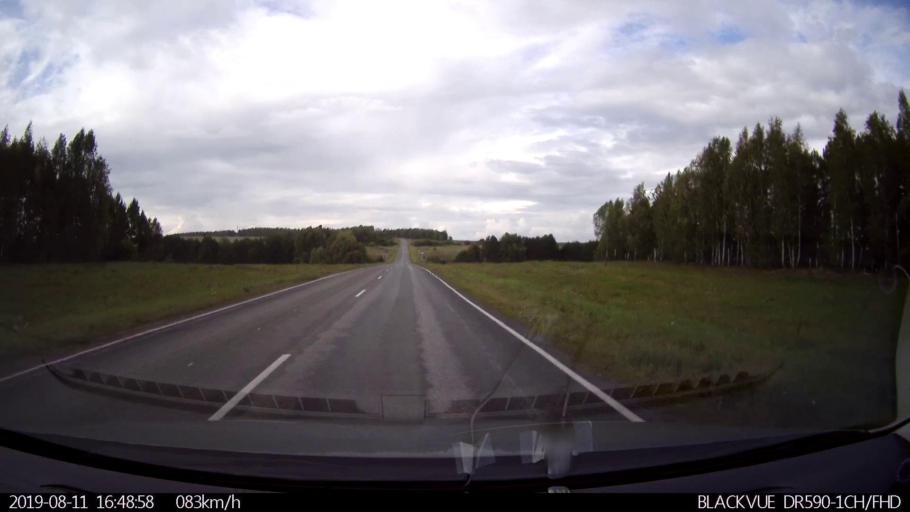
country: RU
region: Ulyanovsk
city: Mayna
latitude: 54.2155
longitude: 47.6942
